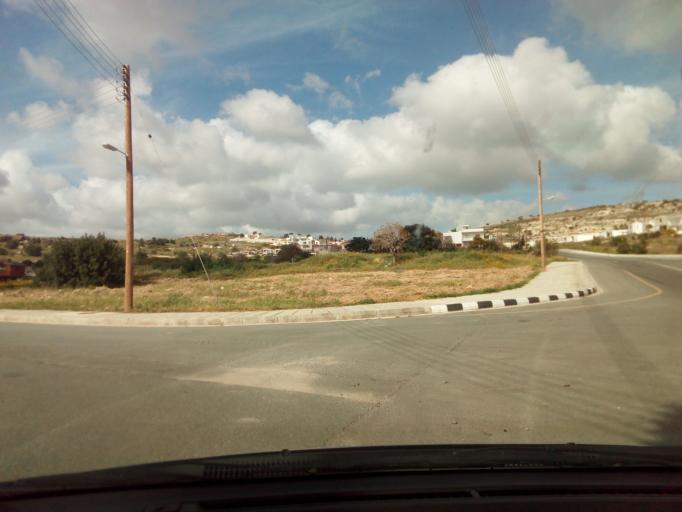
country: CY
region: Pafos
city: Paphos
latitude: 34.7648
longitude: 32.4562
